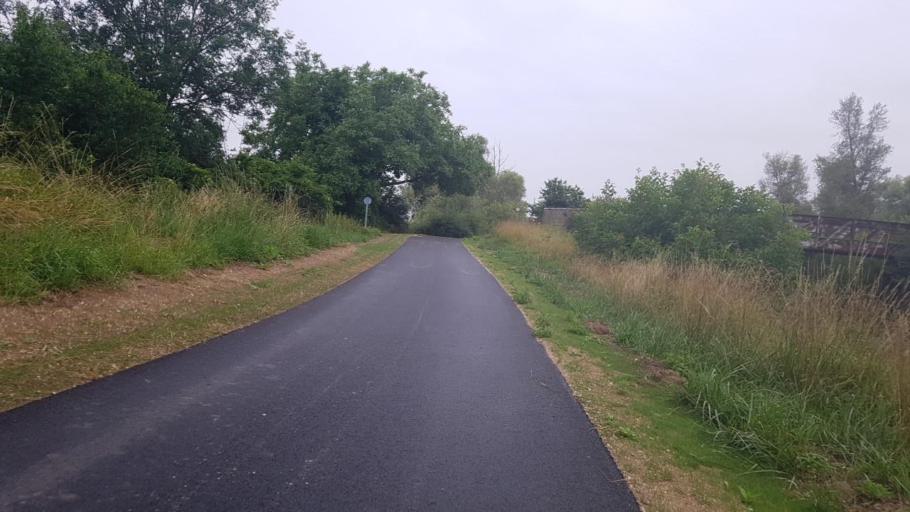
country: FR
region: Champagne-Ardenne
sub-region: Departement de la Marne
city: Vitry-le-Francois
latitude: 48.7799
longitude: 4.5400
